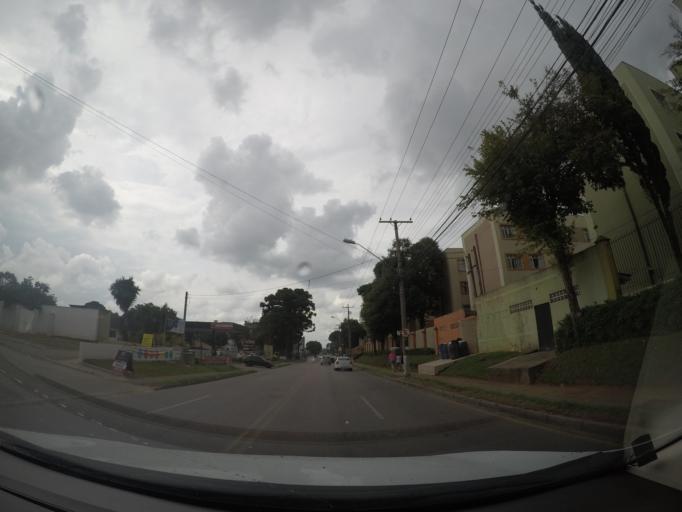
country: BR
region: Parana
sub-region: Sao Jose Dos Pinhais
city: Sao Jose dos Pinhais
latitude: -25.5225
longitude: -49.2413
